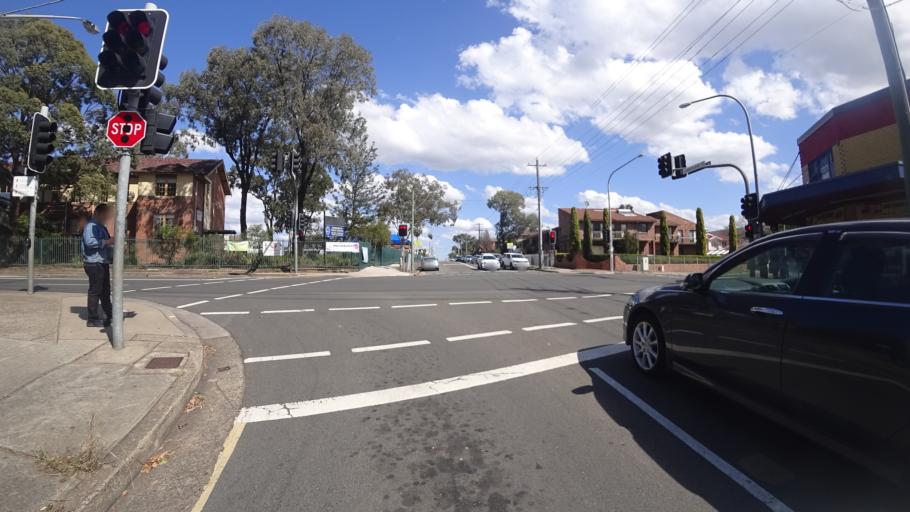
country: AU
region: New South Wales
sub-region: Fairfield
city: Chipping Norton
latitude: -33.8948
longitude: 150.9420
